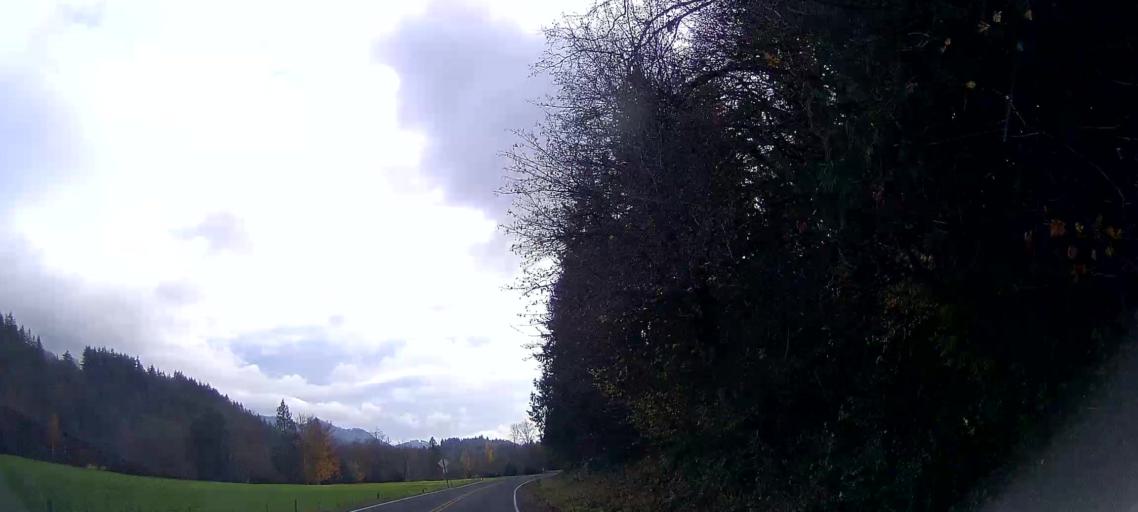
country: US
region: Washington
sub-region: Skagit County
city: Big Lake
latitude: 48.4219
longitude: -122.2106
